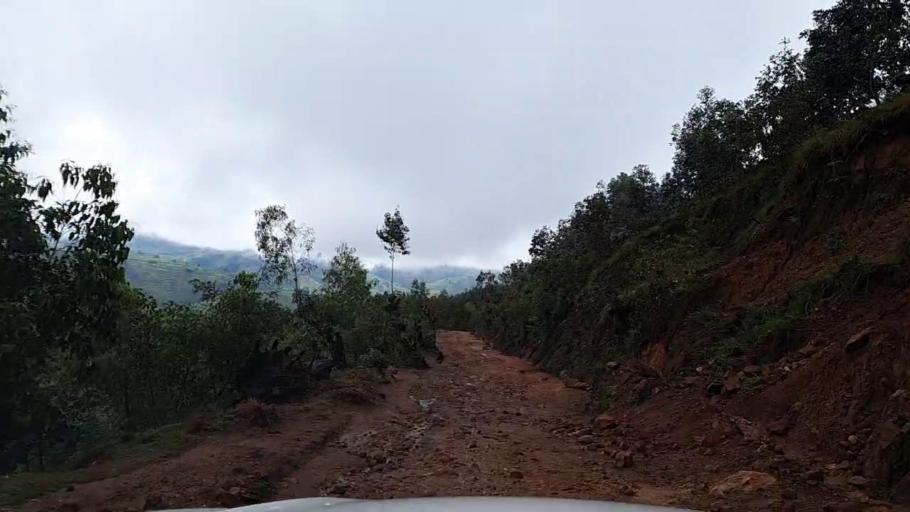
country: RW
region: Southern Province
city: Nzega
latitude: -2.3958
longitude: 29.5001
